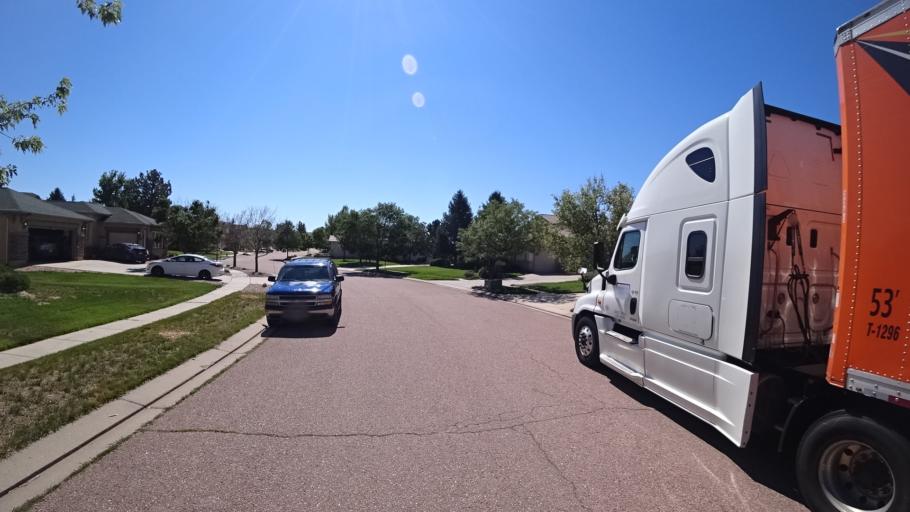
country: US
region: Colorado
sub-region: El Paso County
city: Gleneagle
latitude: 38.9743
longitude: -104.7796
